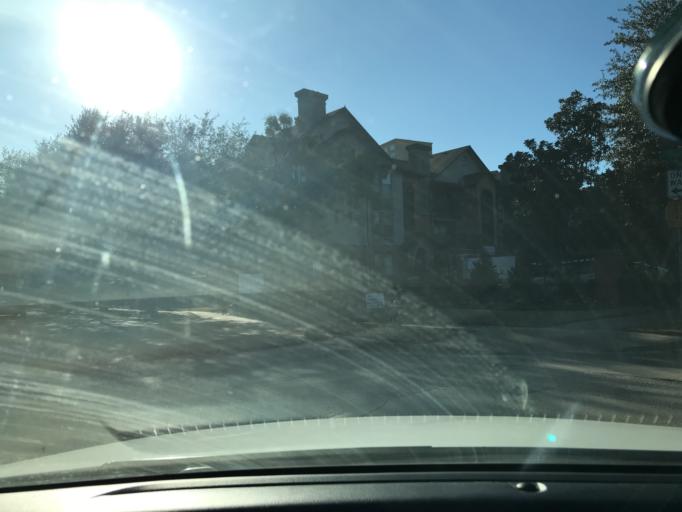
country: US
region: Texas
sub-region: Dallas County
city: Highland Park
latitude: 32.8250
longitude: -96.7876
